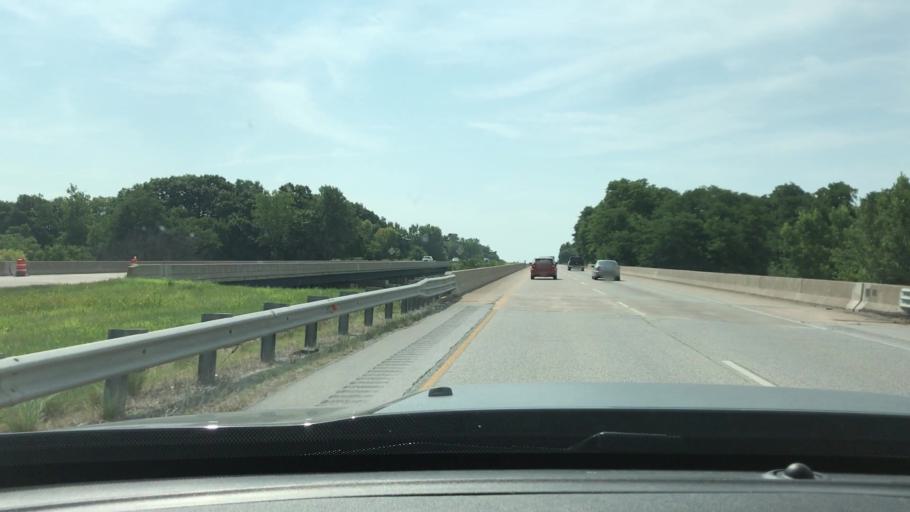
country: US
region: Illinois
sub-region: Henry County
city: Green Rock
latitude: 41.4579
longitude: -90.3788
